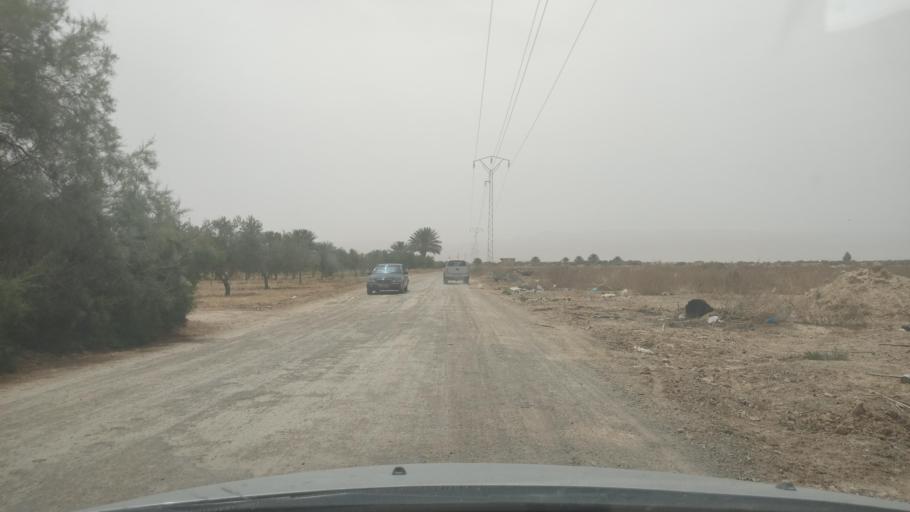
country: TN
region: Gafsa
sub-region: Gafsa Municipality
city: Gafsa
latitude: 34.3214
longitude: 8.9546
